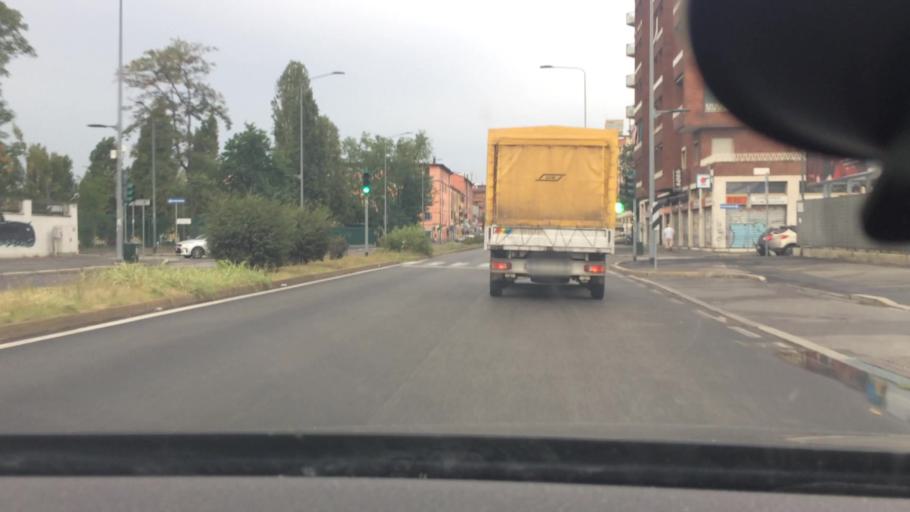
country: IT
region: Lombardy
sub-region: Citta metropolitana di Milano
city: Sesto San Giovanni
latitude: 45.5073
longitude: 9.2232
